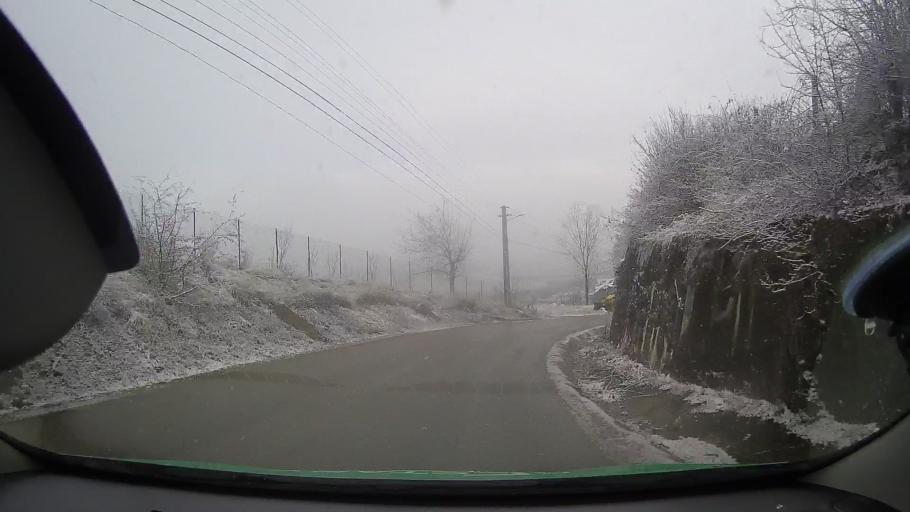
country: RO
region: Alba
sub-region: Oras Ocna Mures
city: Razboieni-Cetate
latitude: 46.3917
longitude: 23.8894
